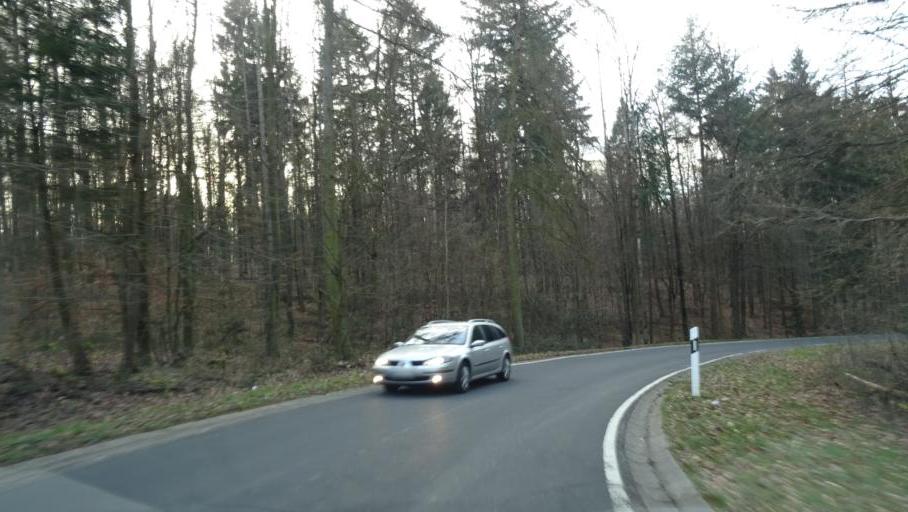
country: DE
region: Baden-Wuerttemberg
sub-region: Karlsruhe Region
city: Mosbach
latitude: 49.3380
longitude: 9.1433
